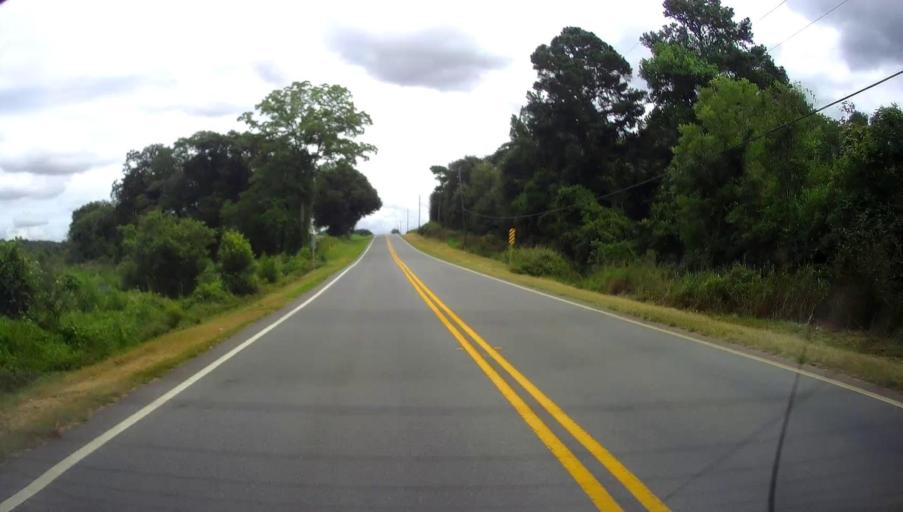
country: US
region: Georgia
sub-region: Macon County
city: Montezuma
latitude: 32.2932
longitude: -83.9912
